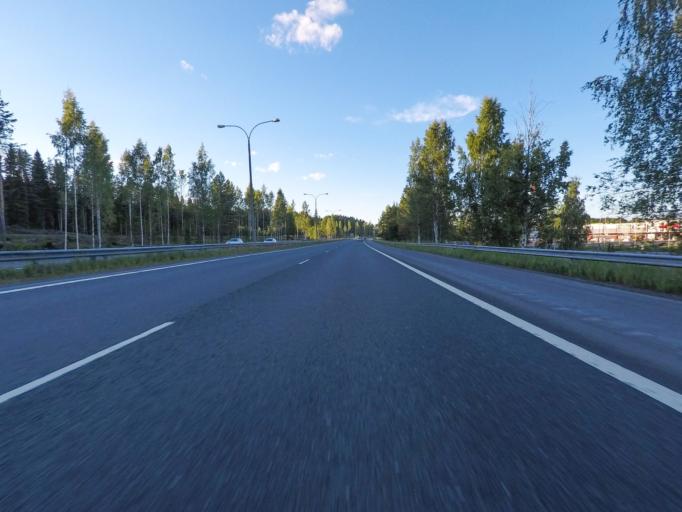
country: FI
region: Northern Savo
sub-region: Kuopio
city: Kuopio
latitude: 62.8708
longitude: 27.6201
